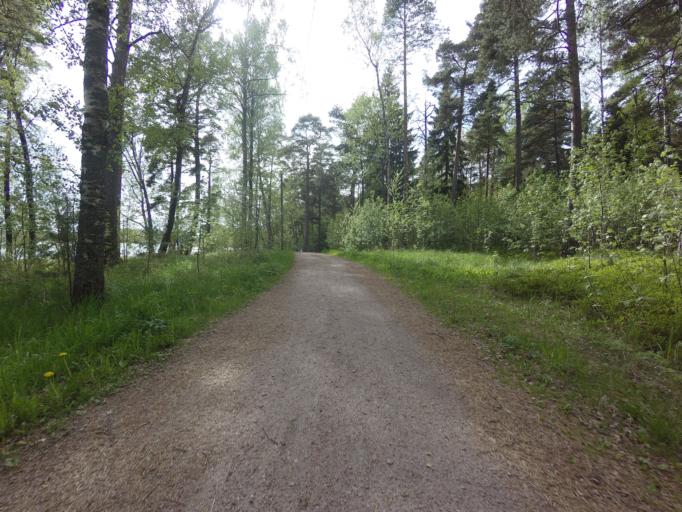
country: FI
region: Uusimaa
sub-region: Helsinki
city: Koukkuniemi
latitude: 60.1284
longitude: 24.6930
